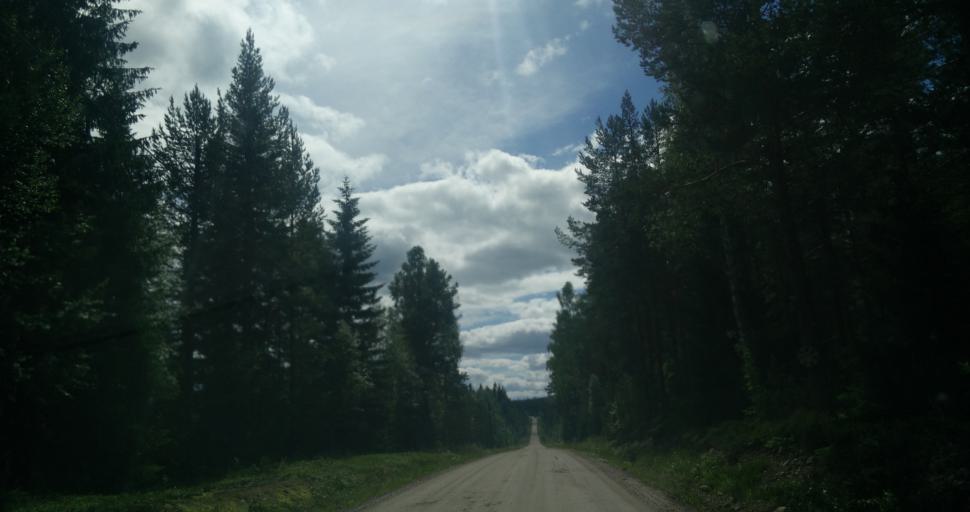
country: SE
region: Vaesternorrland
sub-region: Sundsvalls Kommun
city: Vi
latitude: 62.1455
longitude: 17.1351
